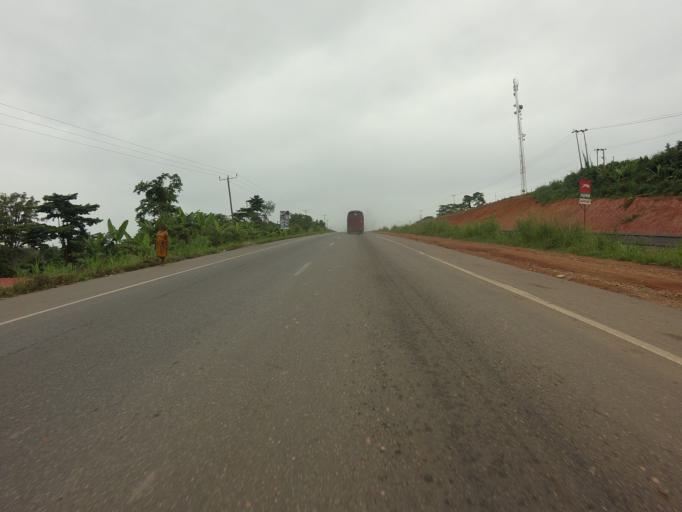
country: GH
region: Eastern
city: Suhum
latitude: 6.0481
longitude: -0.4607
